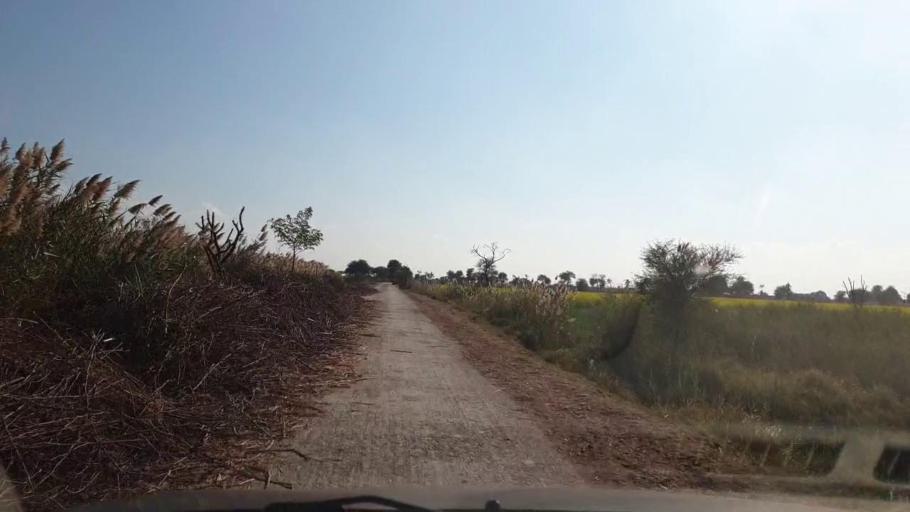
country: PK
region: Sindh
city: Sinjhoro
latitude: 25.9999
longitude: 68.7311
